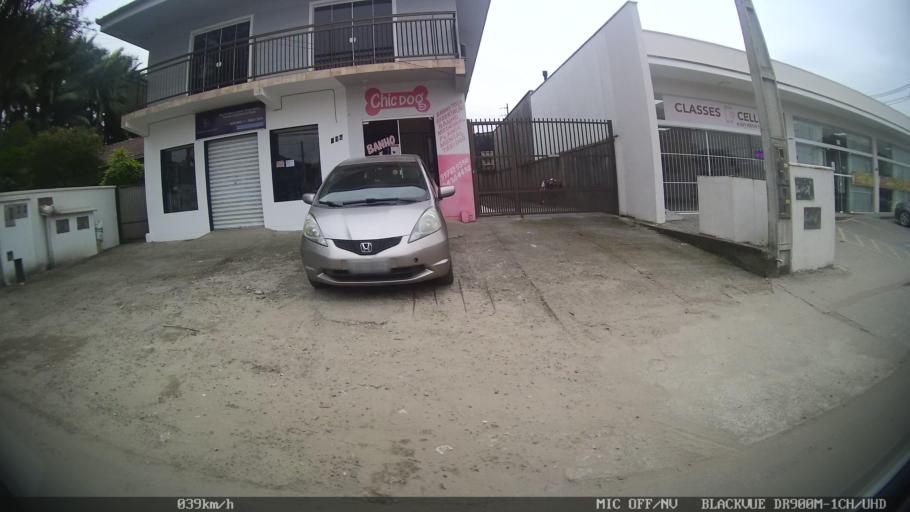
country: BR
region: Santa Catarina
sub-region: Joinville
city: Joinville
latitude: -26.3503
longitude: -48.7959
